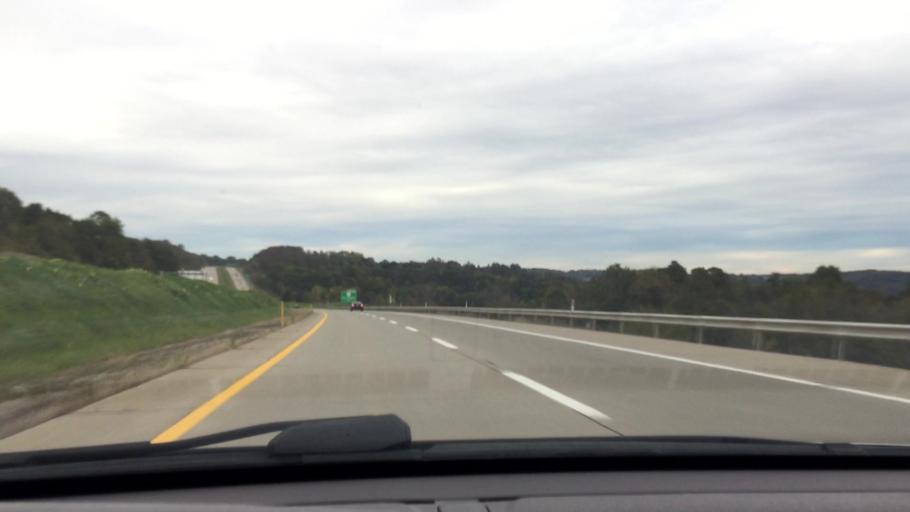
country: US
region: Pennsylvania
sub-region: Lawrence County
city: Oakland
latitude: 40.9508
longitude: -80.3922
